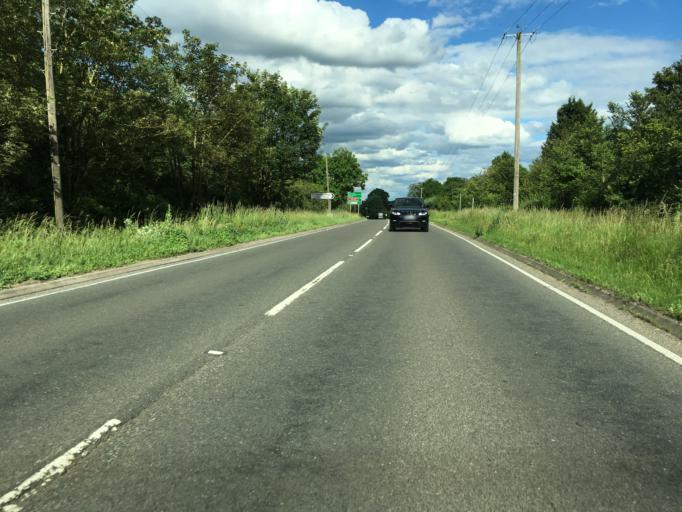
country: GB
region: England
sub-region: Oxfordshire
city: Wheatley
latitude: 51.7383
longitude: -1.0858
